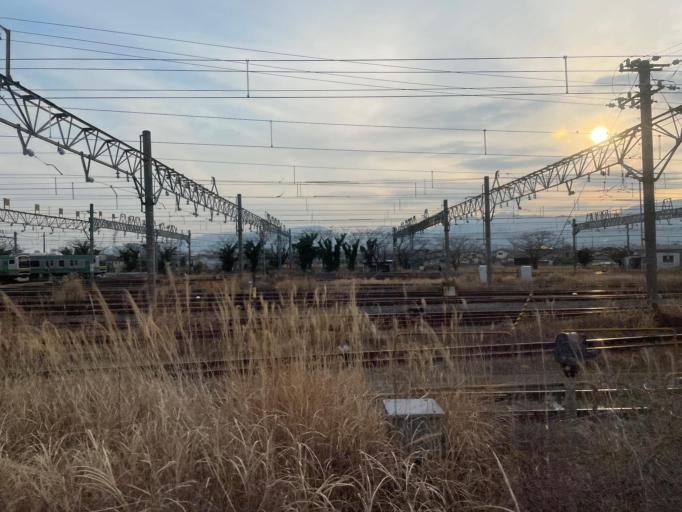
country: JP
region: Kanagawa
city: Odawara
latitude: 35.2941
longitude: 139.1936
